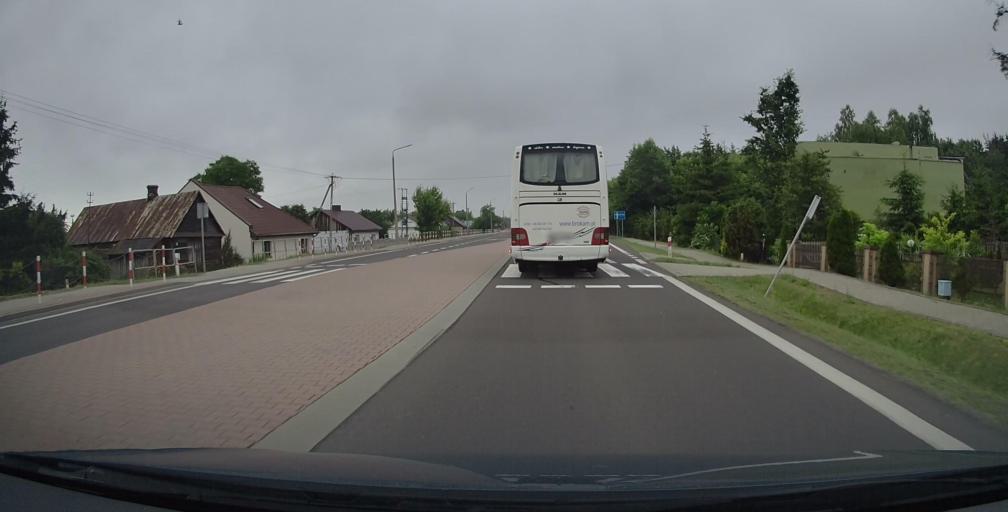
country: PL
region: Lublin Voivodeship
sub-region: Powiat bialski
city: Terespol
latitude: 52.0398
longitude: 23.5131
